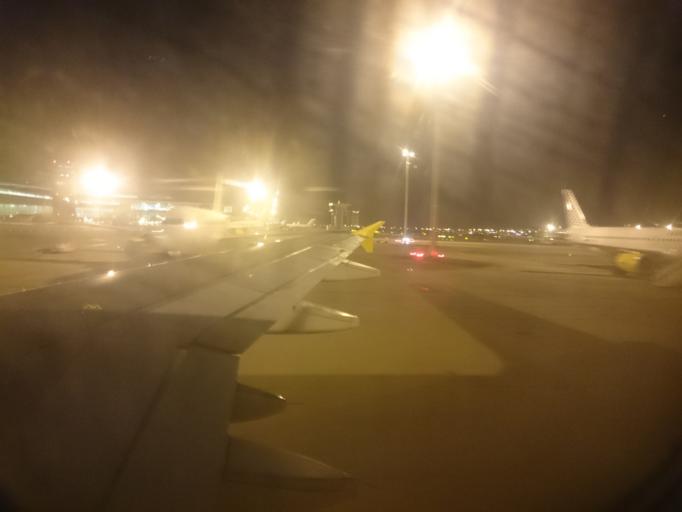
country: ES
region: Catalonia
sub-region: Provincia de Barcelona
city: El Prat de Llobregat
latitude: 41.2931
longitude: 2.0790
